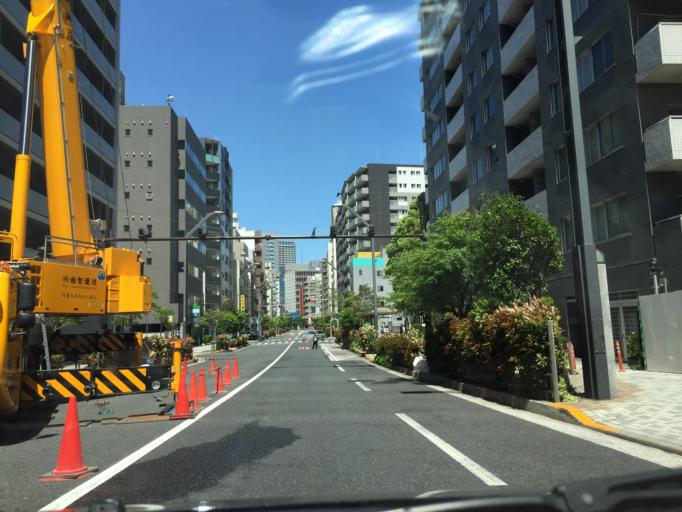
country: JP
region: Tokyo
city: Tokyo
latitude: 35.6731
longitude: 139.7834
